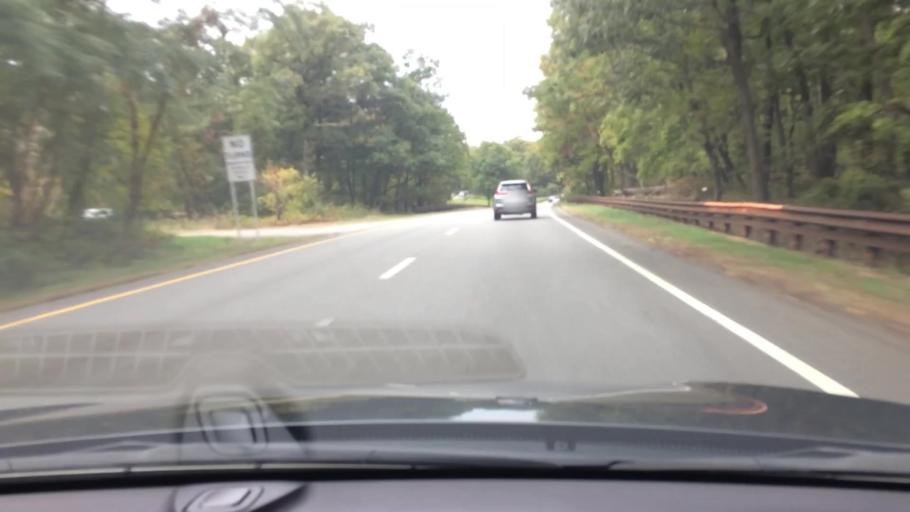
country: US
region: New Jersey
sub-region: Bergen County
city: Tenafly
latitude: 40.9138
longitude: -73.9348
